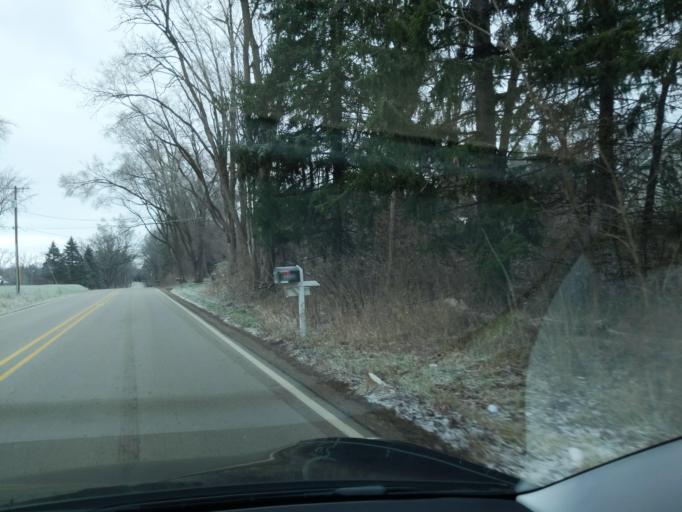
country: US
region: Michigan
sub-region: Jackson County
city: Spring Arbor
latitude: 42.2259
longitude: -84.5168
